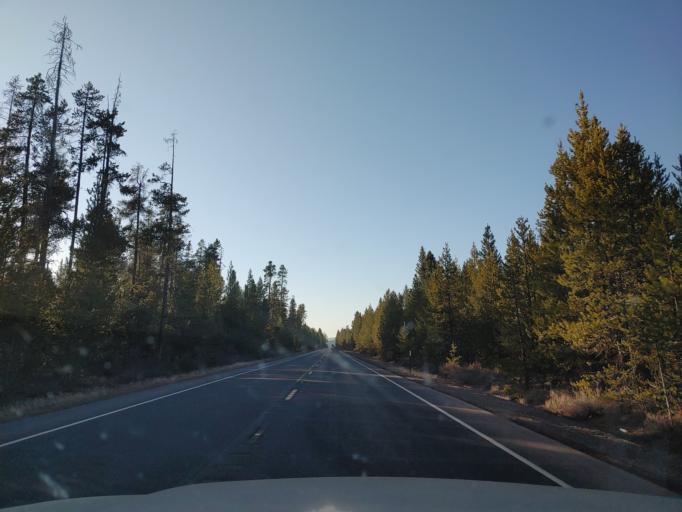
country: US
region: Oregon
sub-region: Deschutes County
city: La Pine
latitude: 43.3858
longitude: -121.8065
